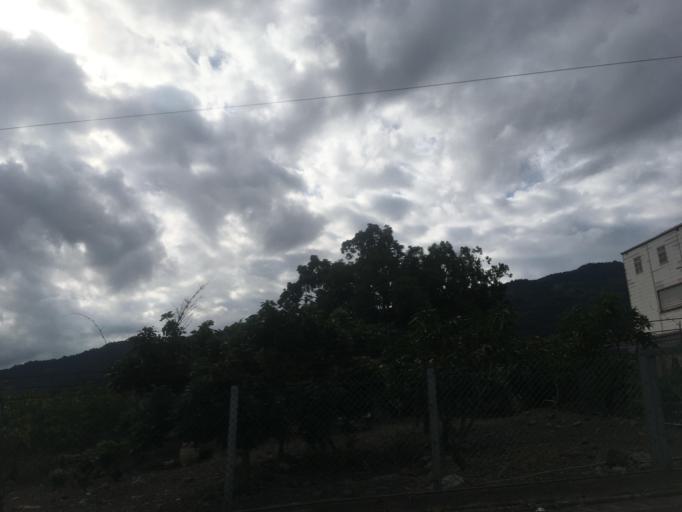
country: TW
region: Taiwan
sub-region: Yilan
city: Yilan
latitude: 24.6704
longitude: 121.6628
